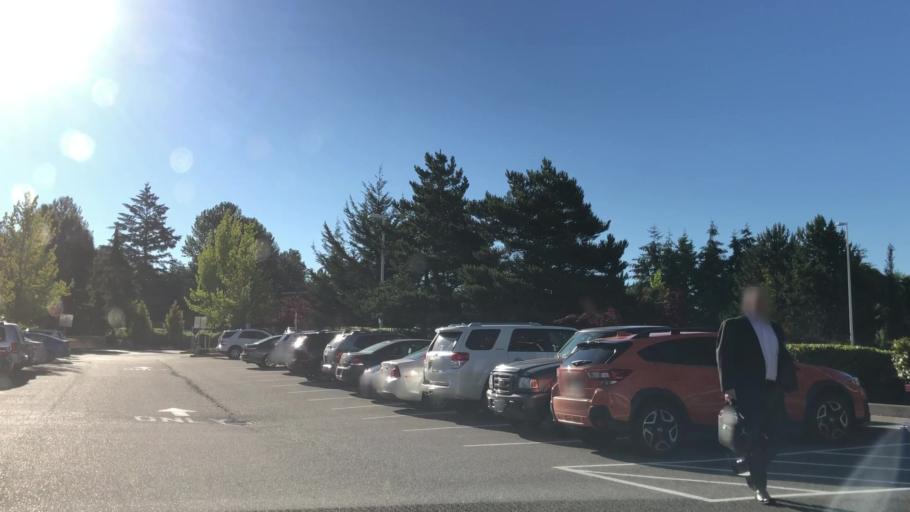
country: US
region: Washington
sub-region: Snohomish County
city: Mukilteo
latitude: 47.9312
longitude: -122.2629
